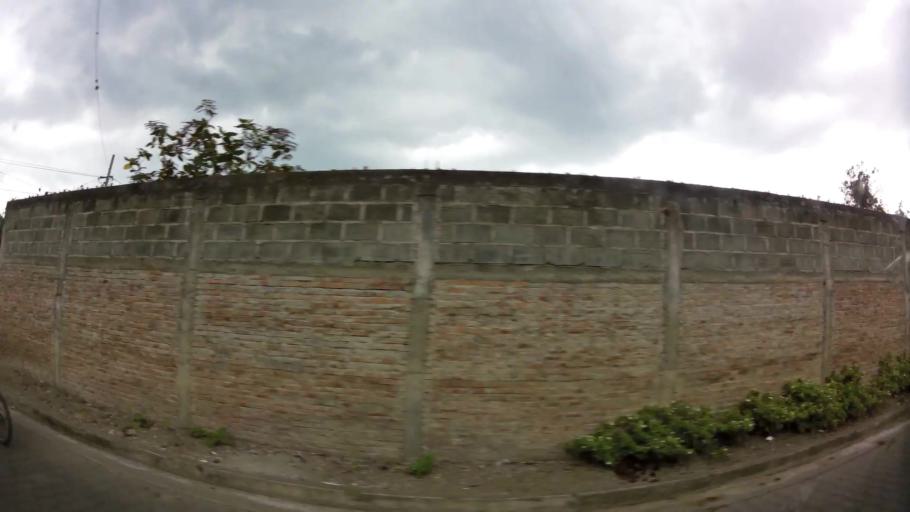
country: NI
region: Jinotega
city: Jinotega
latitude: 13.0932
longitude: -86.0046
